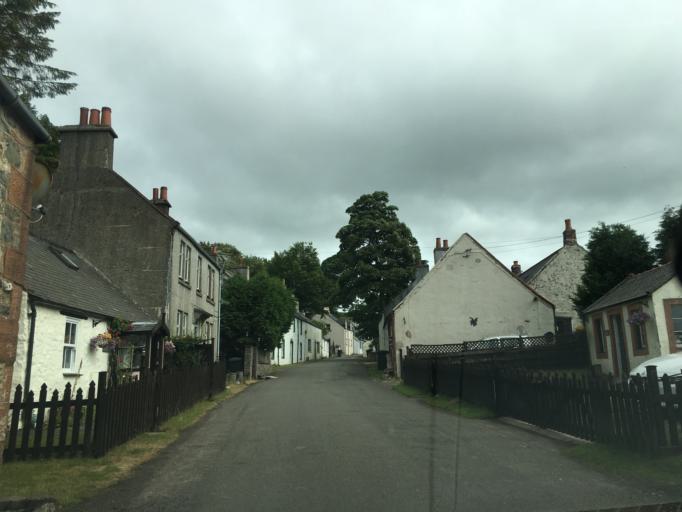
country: GB
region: Scotland
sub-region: Dumfries and Galloway
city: Sanquhar
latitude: 55.3987
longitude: -3.7841
